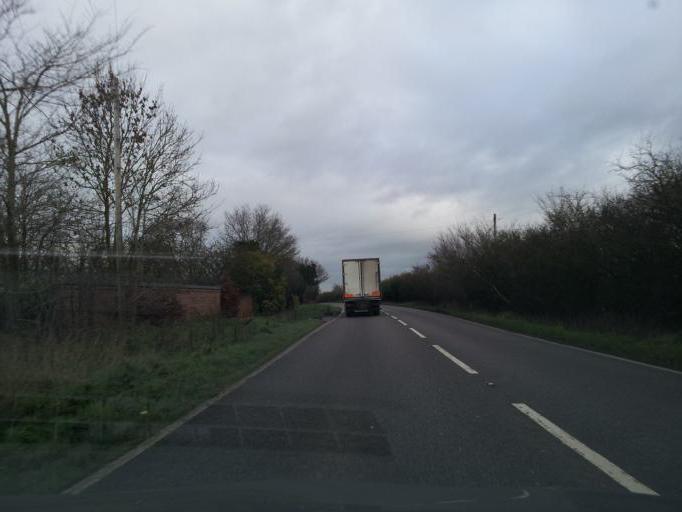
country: GB
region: England
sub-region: Norfolk
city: Diss
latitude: 52.3513
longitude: 1.1381
